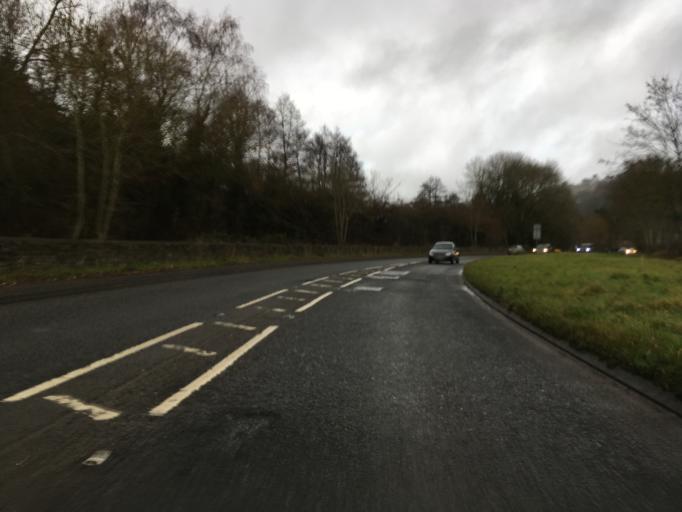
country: GB
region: England
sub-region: Gloucestershire
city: Nailsworth
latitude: 51.7195
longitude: -2.2304
